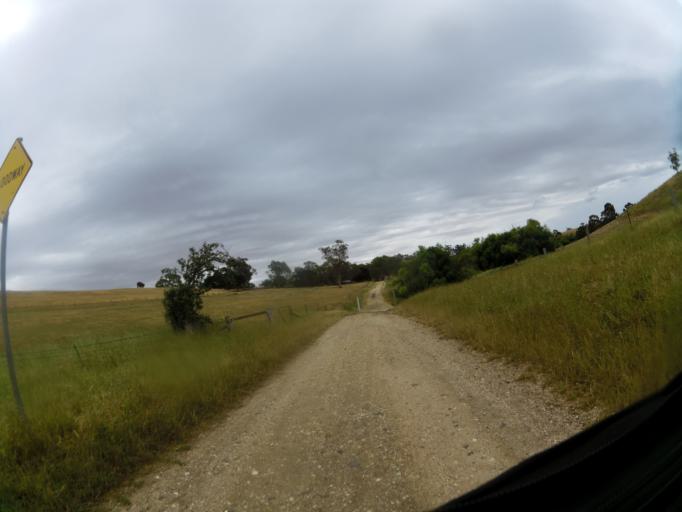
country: AU
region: Victoria
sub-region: Mount Alexander
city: Castlemaine
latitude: -37.2018
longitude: 144.0166
